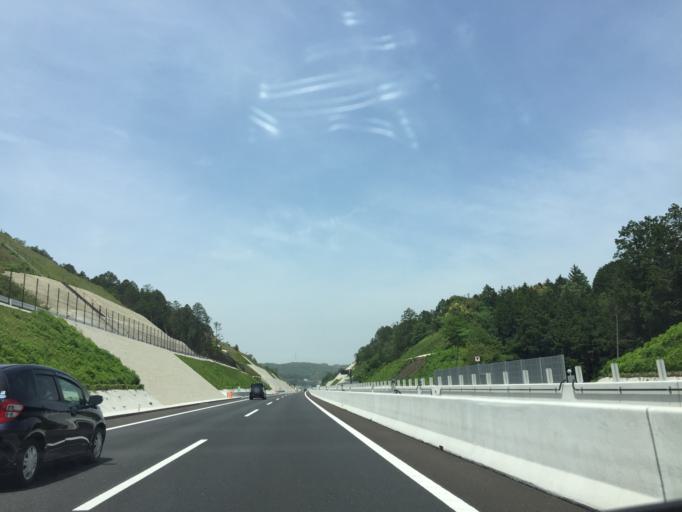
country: JP
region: Aichi
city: Gamagori
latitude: 34.9070
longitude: 137.3004
